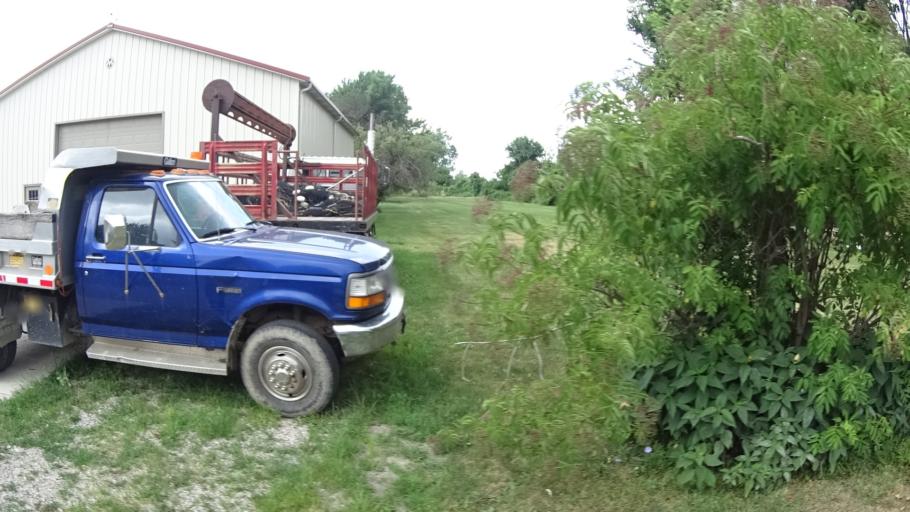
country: US
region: Ohio
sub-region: Erie County
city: Sandusky
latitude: 41.4477
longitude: -82.7715
